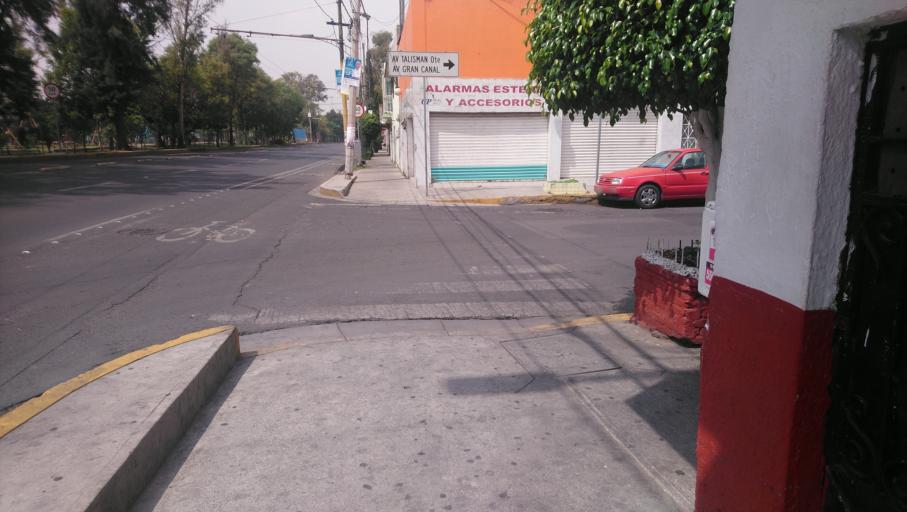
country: MX
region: Mexico City
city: Gustavo A. Madero
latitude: 19.4704
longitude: -99.1018
